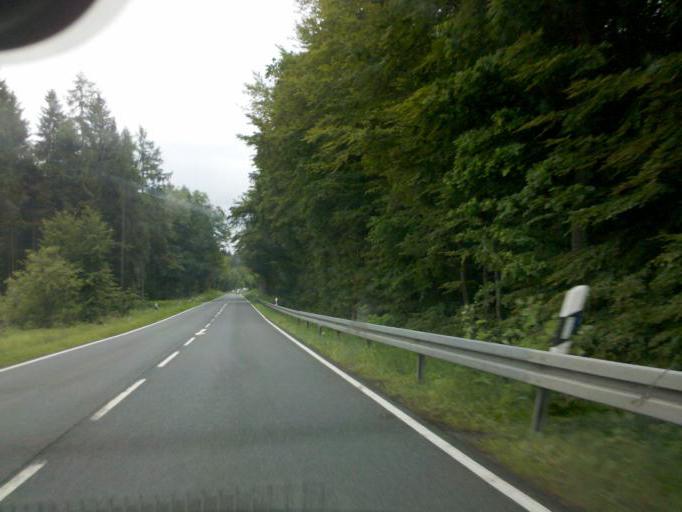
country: DE
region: North Rhine-Westphalia
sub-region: Regierungsbezirk Arnsberg
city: Wilnsdorf
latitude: 50.7917
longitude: 8.1464
